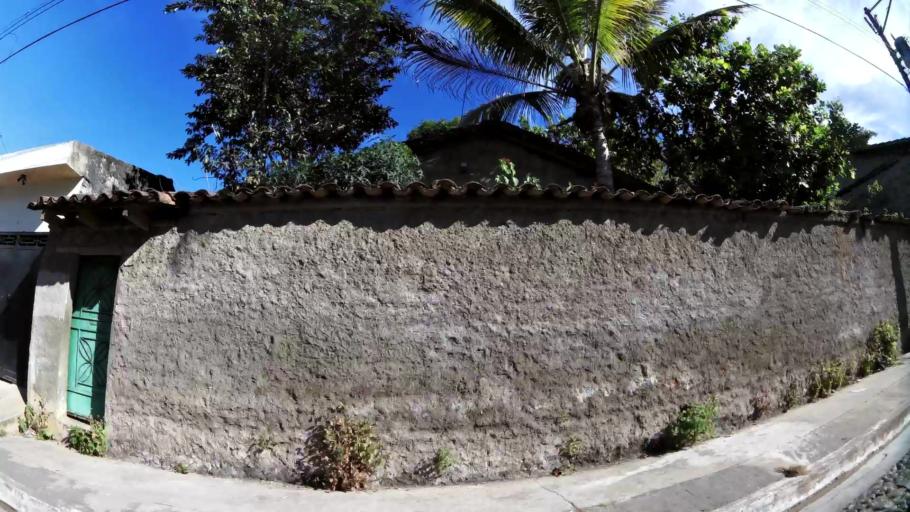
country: SV
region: Cuscatlan
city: Suchitoto
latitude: 13.9352
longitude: -89.0282
